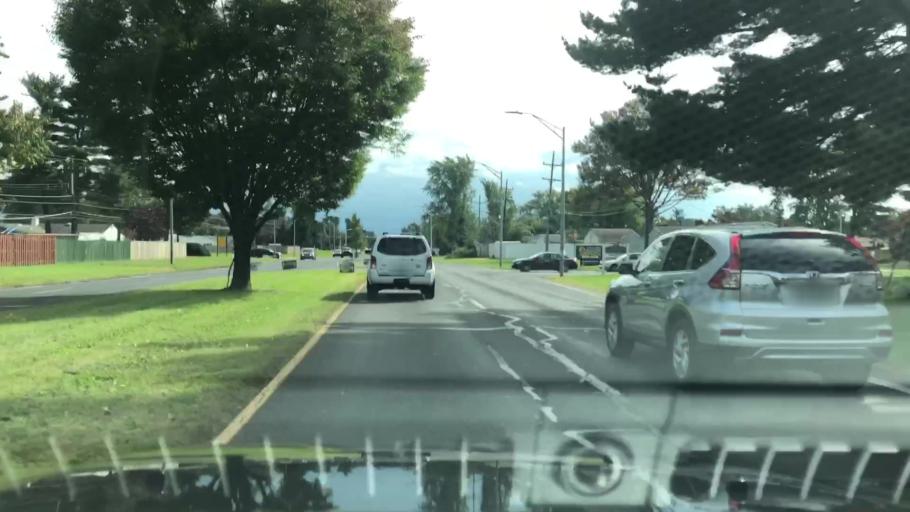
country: US
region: Pennsylvania
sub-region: Bucks County
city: Levittown
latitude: 40.1583
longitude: -74.8308
